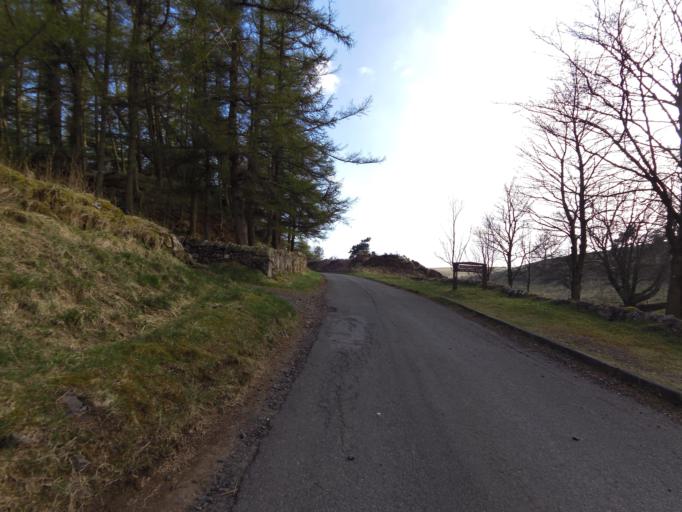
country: GB
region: Scotland
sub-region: Fife
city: Falkland
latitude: 56.2417
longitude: -3.2476
